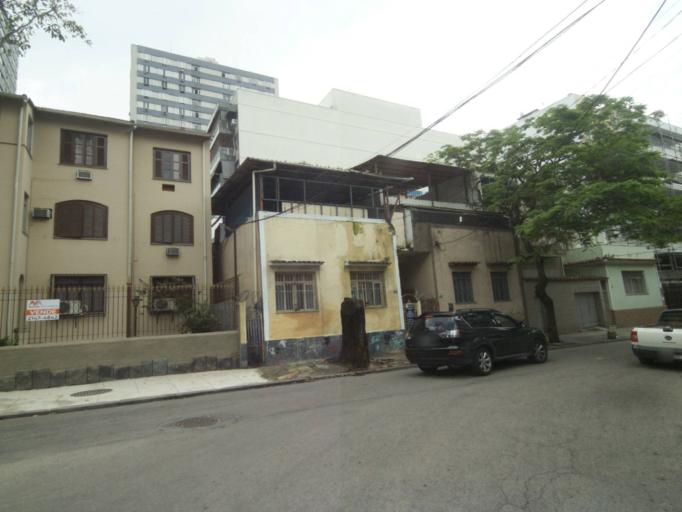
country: BR
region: Rio de Janeiro
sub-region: Rio De Janeiro
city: Rio de Janeiro
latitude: -22.9340
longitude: -43.2459
